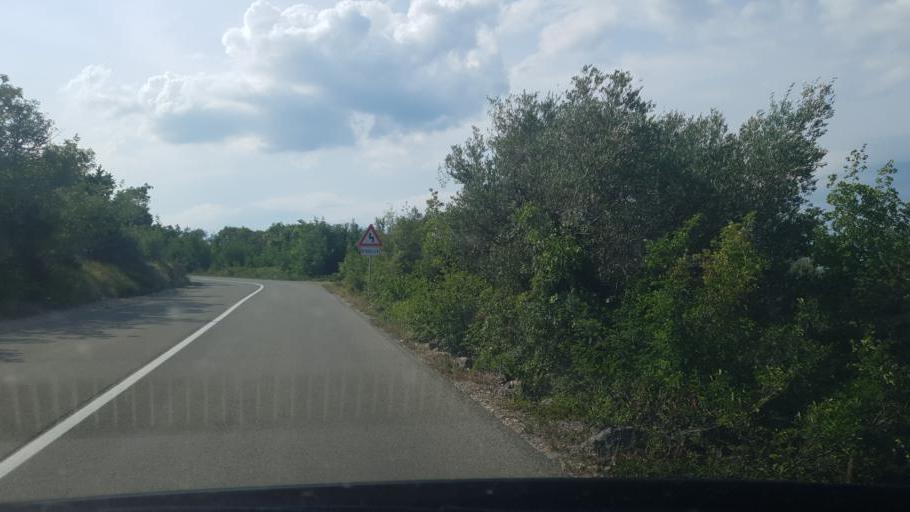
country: HR
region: Primorsko-Goranska
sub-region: Grad Crikvenica
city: Crikvenica
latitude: 45.1071
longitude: 14.6425
